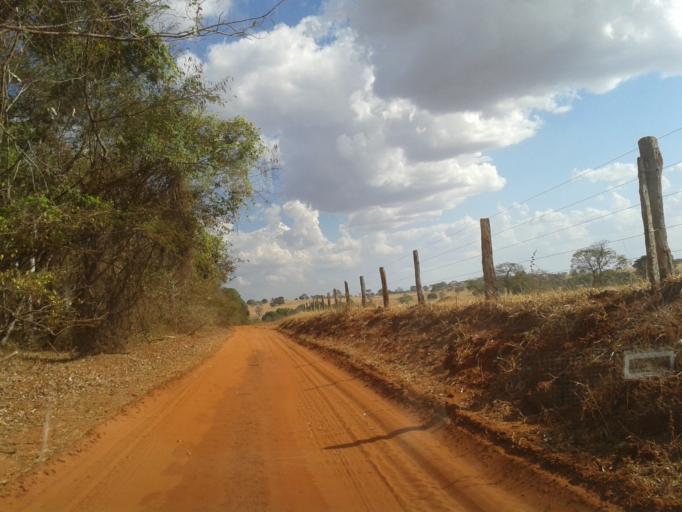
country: BR
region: Minas Gerais
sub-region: Santa Vitoria
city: Santa Vitoria
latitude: -19.2650
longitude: -49.9876
